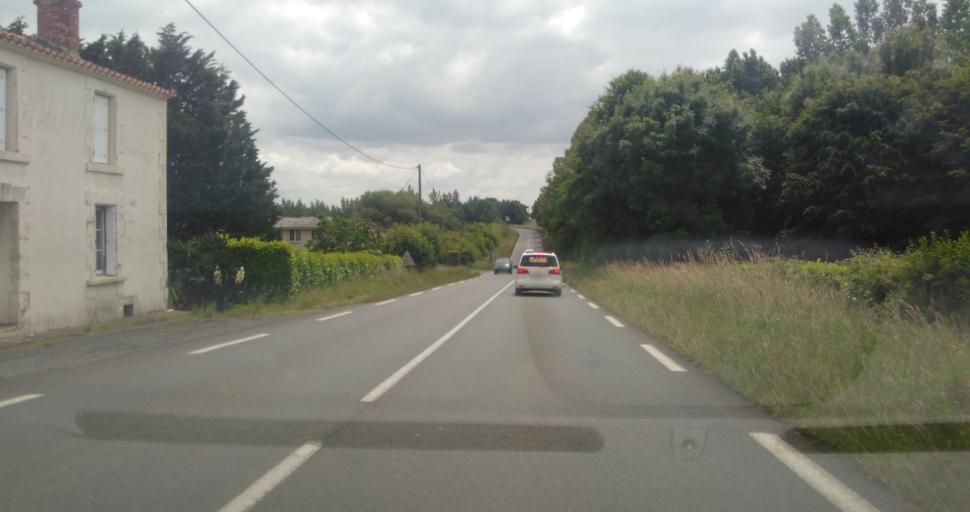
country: FR
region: Pays de la Loire
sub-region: Departement de la Vendee
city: Bournezeau
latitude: 46.5989
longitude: -1.1323
